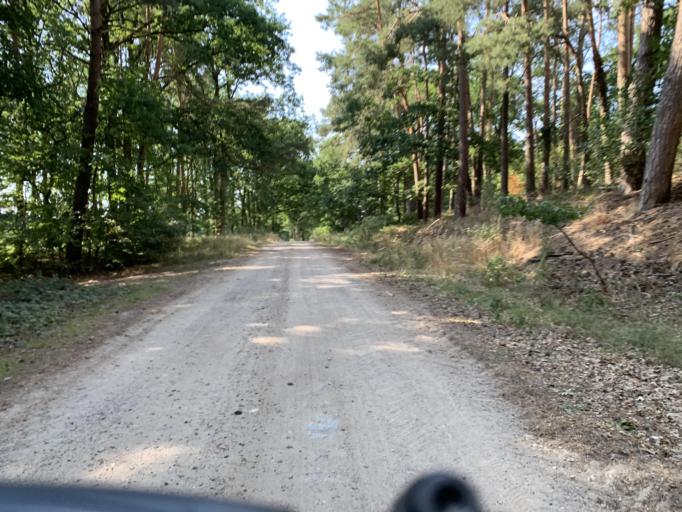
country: DE
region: Lower Saxony
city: Thomasburg
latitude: 53.2347
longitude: 10.6361
